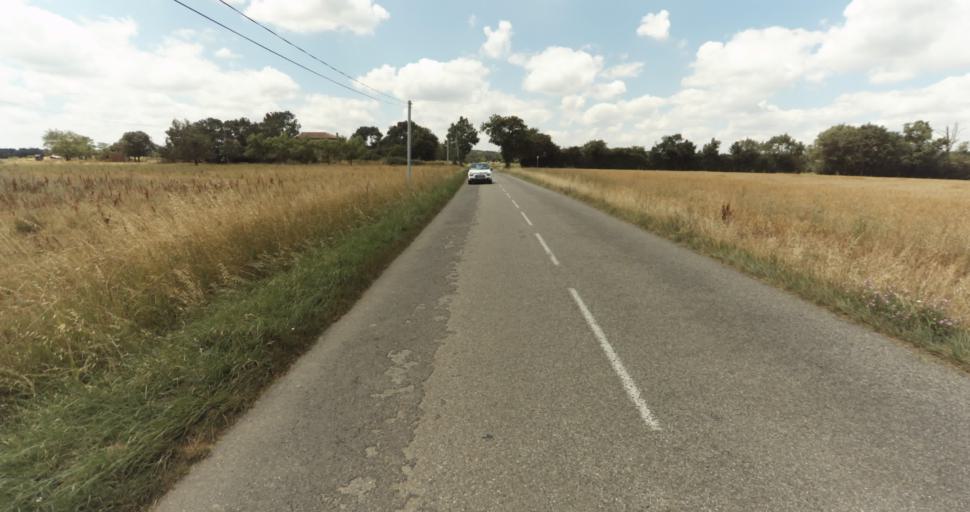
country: FR
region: Midi-Pyrenees
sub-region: Departement de la Haute-Garonne
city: Fontenilles
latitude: 43.5472
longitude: 1.1784
